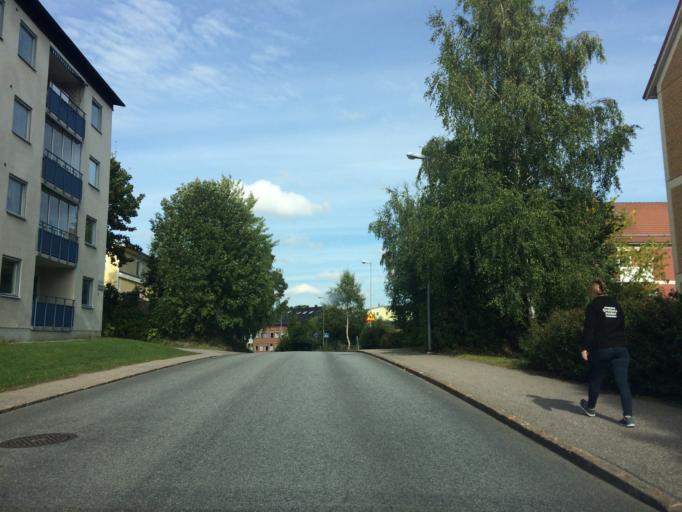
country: SE
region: Stockholm
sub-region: Sollentuna Kommun
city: Sollentuna
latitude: 59.4468
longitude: 17.9348
